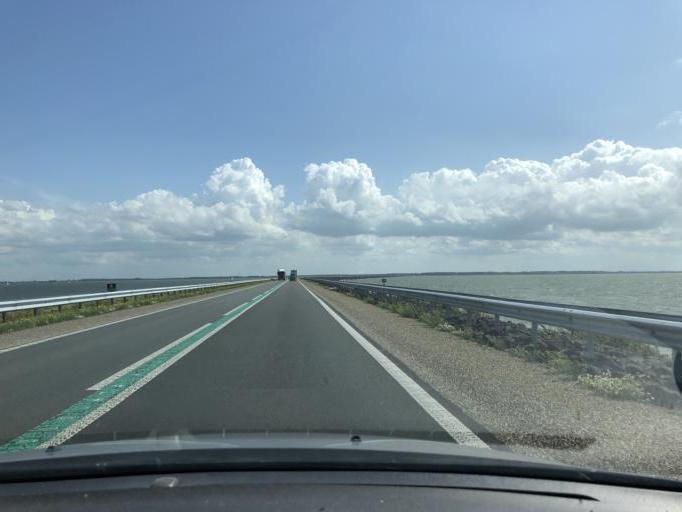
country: NL
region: Flevoland
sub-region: Gemeente Lelystad
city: Lelystad
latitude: 52.5981
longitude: 5.4513
